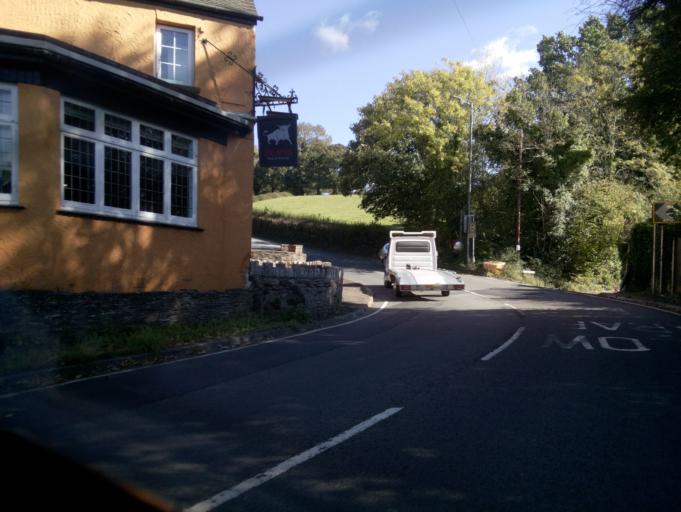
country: GB
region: Wales
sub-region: Newport
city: Caerleon
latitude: 51.6030
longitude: -2.9484
